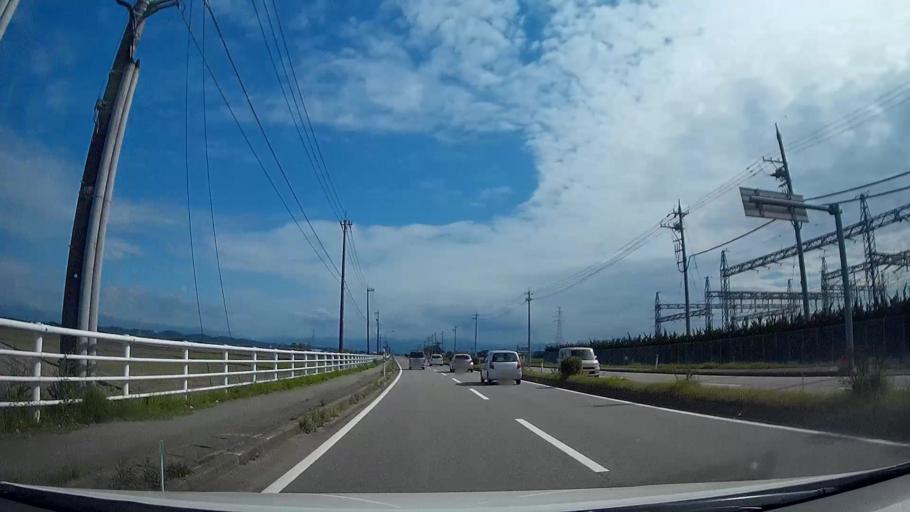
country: JP
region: Toyama
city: Kuragaki-kosugi
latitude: 36.7465
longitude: 137.1294
